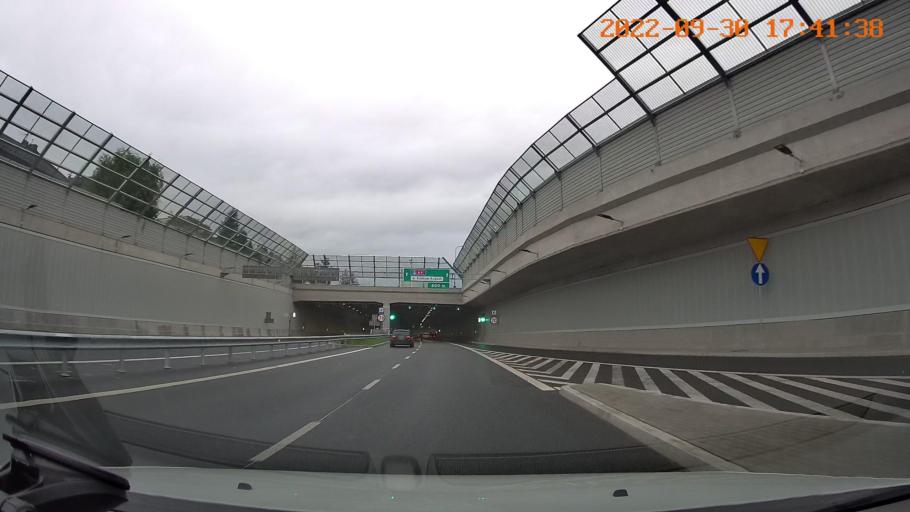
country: PL
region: Lesser Poland Voivodeship
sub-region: Krakow
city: Krakow
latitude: 50.0217
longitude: 19.9306
